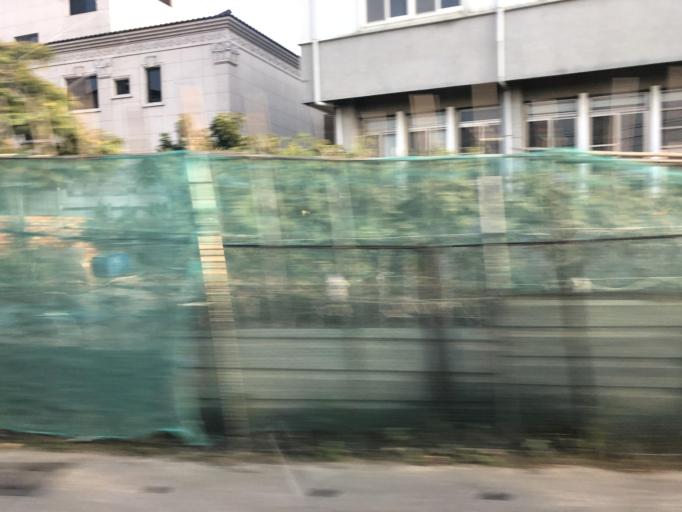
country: TW
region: Taiwan
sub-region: Tainan
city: Tainan
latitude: 23.1343
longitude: 120.2596
